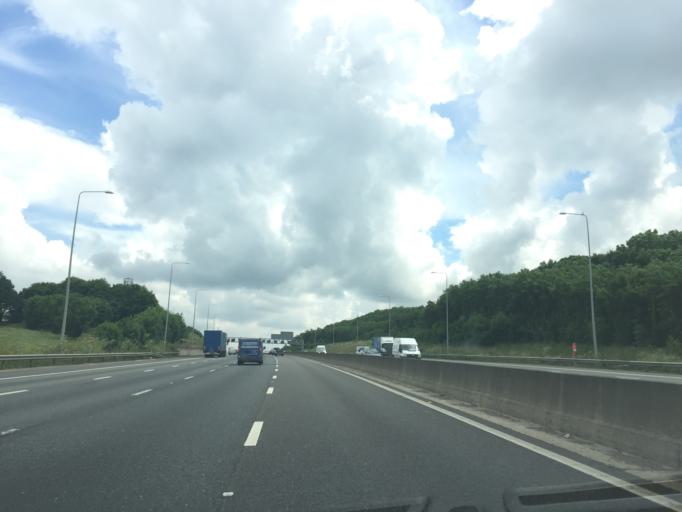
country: GB
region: England
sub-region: Hertfordshire
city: Shenley AV
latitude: 51.7106
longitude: -0.2622
